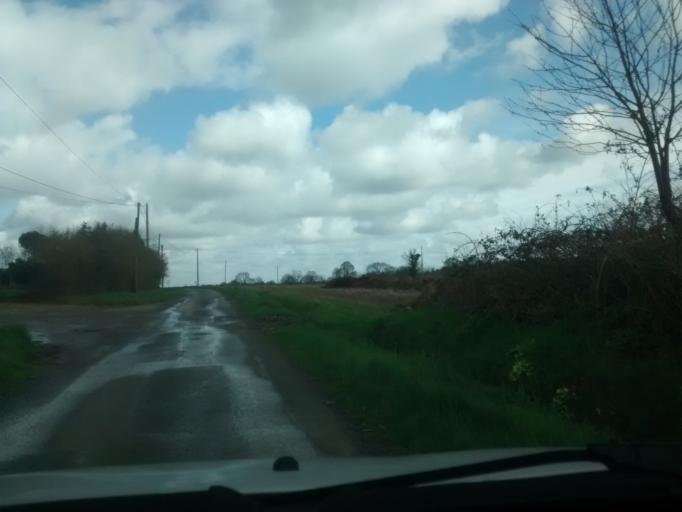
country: FR
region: Brittany
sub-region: Departement d'Ille-et-Vilaine
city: Servon-sur-Vilaine
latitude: 48.1519
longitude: -1.4911
